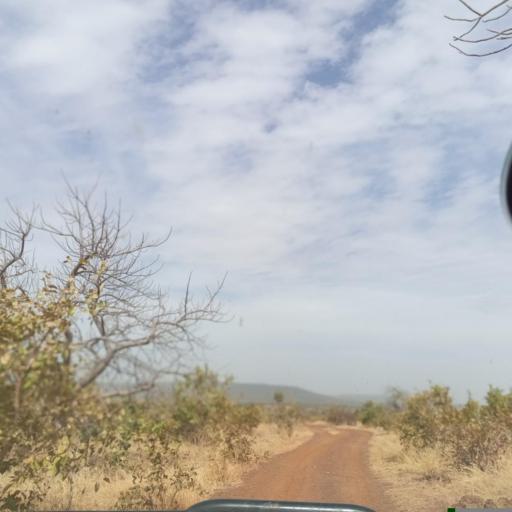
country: ML
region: Koulikoro
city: Koulikoro
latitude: 13.1596
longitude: -7.7266
